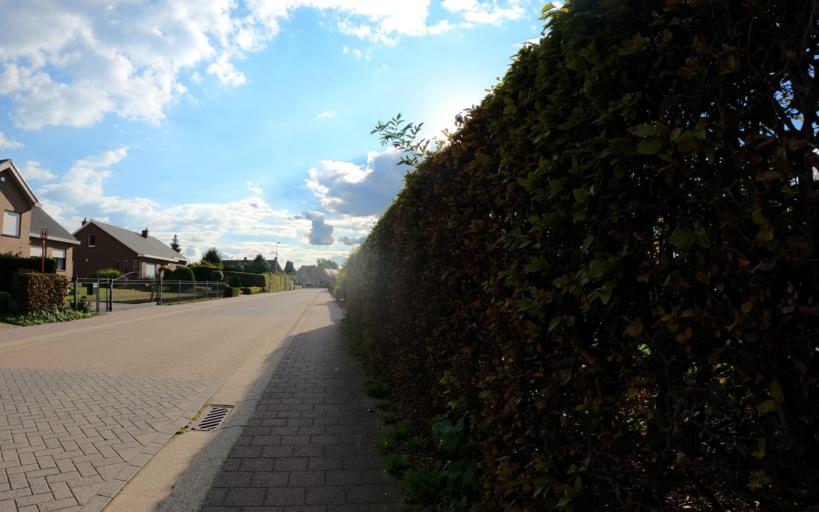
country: BE
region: Flanders
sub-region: Provincie Antwerpen
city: Oostmalle
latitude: 51.3081
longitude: 4.7434
